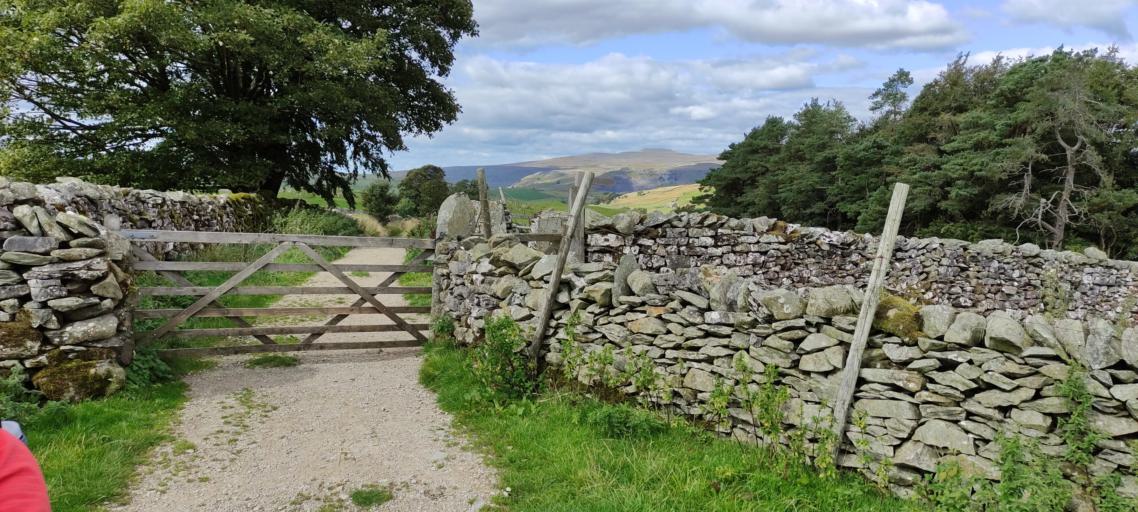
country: GB
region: England
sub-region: North Yorkshire
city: Settle
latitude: 54.0986
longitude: -2.2584
